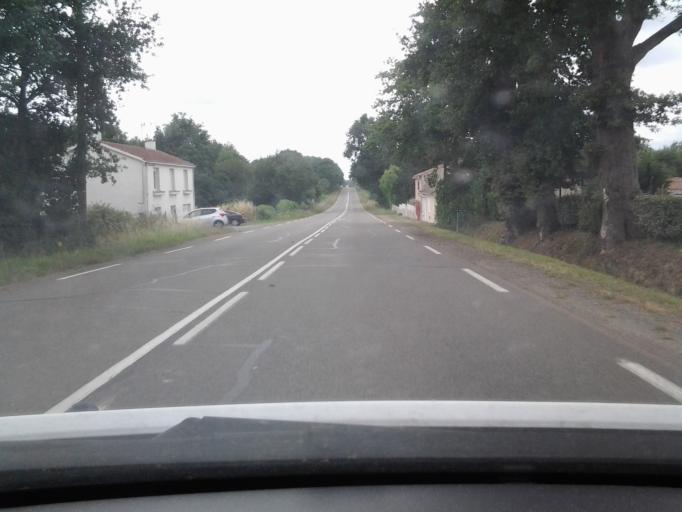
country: FR
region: Pays de la Loire
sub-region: Departement de la Vendee
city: La Roche-sur-Yon
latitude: 46.6607
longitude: -1.4677
